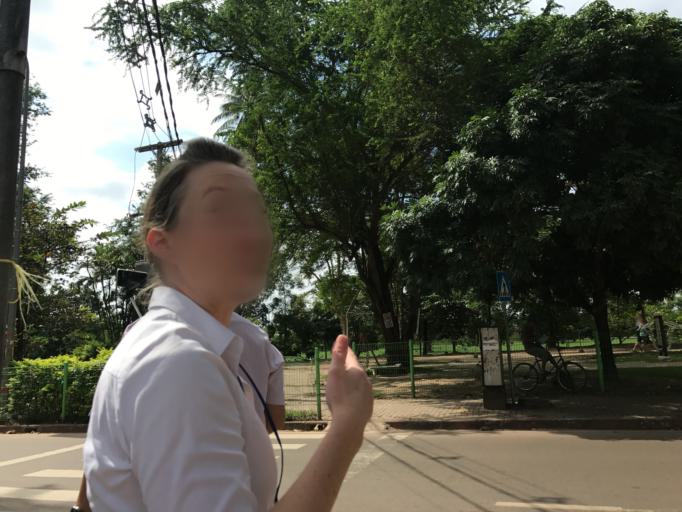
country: LA
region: Vientiane
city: Vientiane
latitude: 17.9621
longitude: 102.6086
